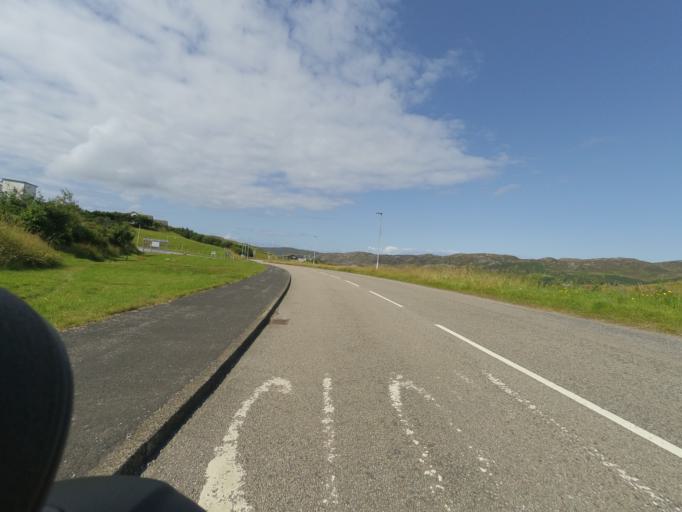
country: GB
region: Scotland
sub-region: Highland
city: Ullapool
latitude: 58.3449
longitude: -5.1590
